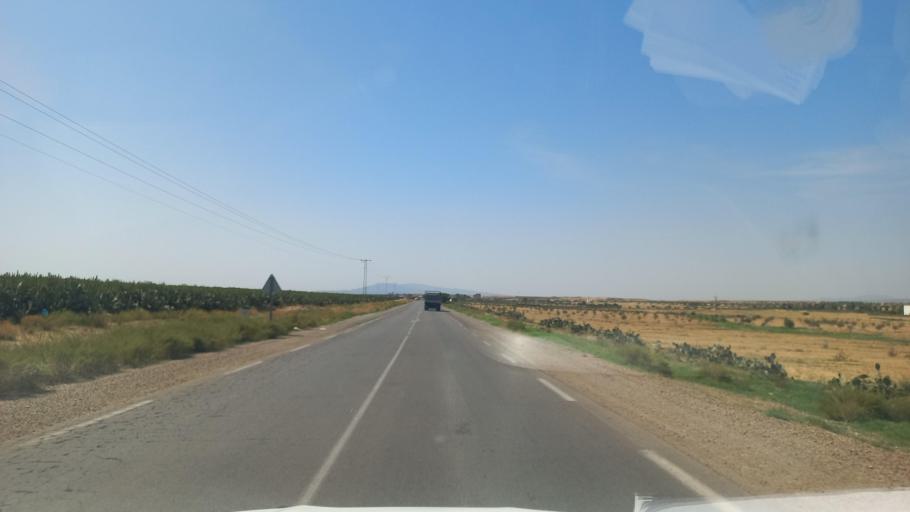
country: TN
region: Al Qasrayn
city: Sbiba
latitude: 35.3726
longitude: 9.0994
